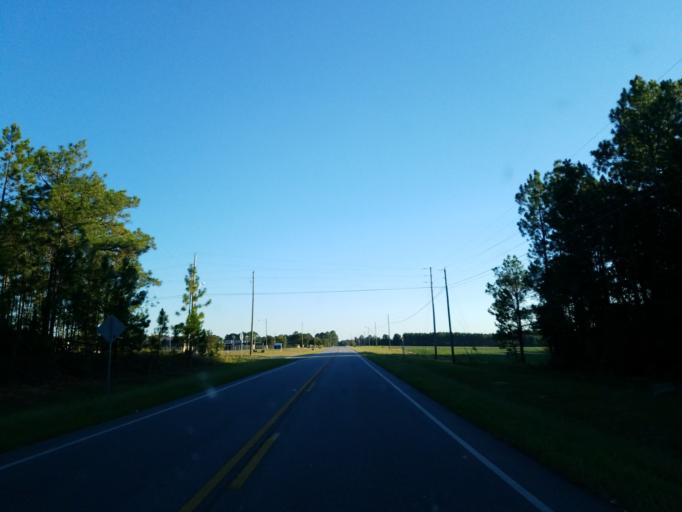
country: US
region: Georgia
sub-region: Worth County
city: Sylvester
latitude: 31.5517
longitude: -83.8430
